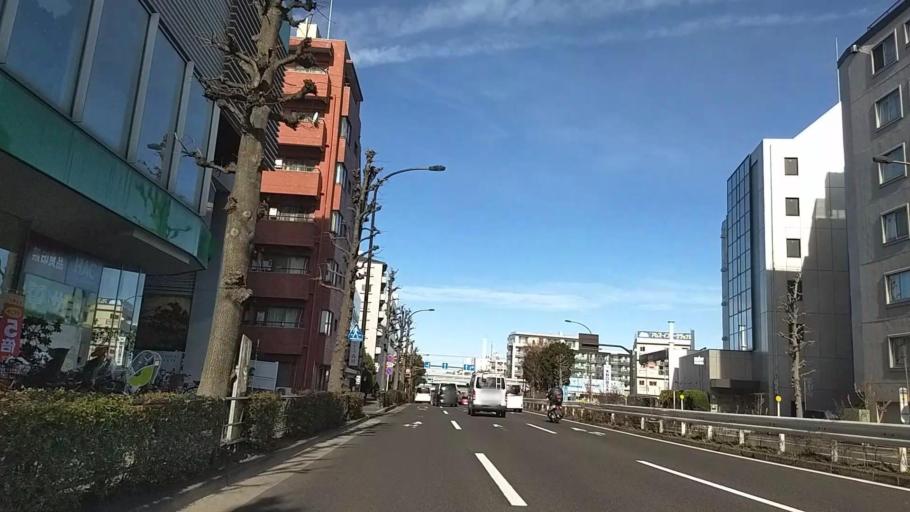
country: JP
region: Tokyo
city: Mitaka-shi
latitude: 35.6438
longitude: 139.6184
